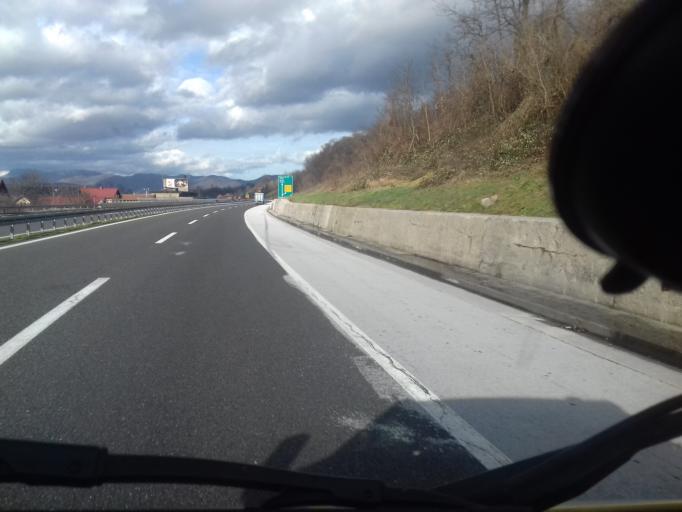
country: BA
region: Federation of Bosnia and Herzegovina
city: Visoko
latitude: 43.9993
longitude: 18.1820
